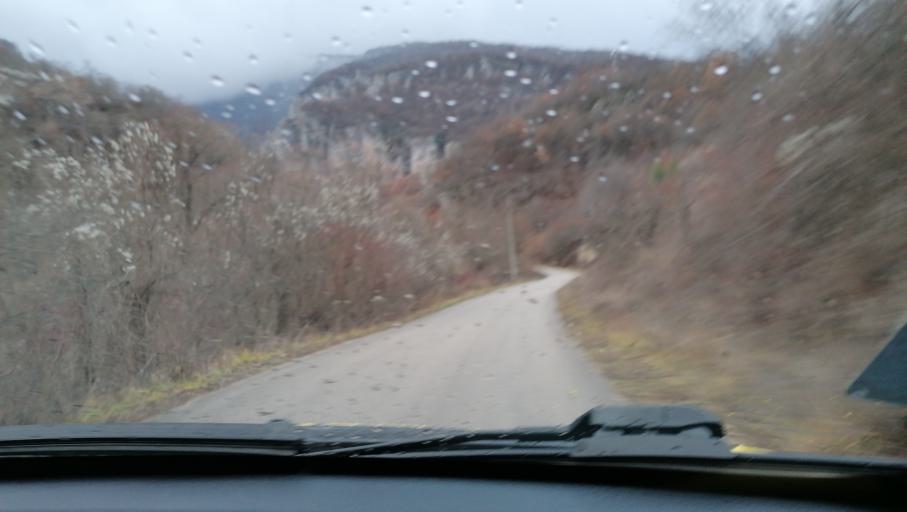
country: RS
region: Central Serbia
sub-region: Pirotski Okrug
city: Dimitrovgrad
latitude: 42.9815
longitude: 22.6426
